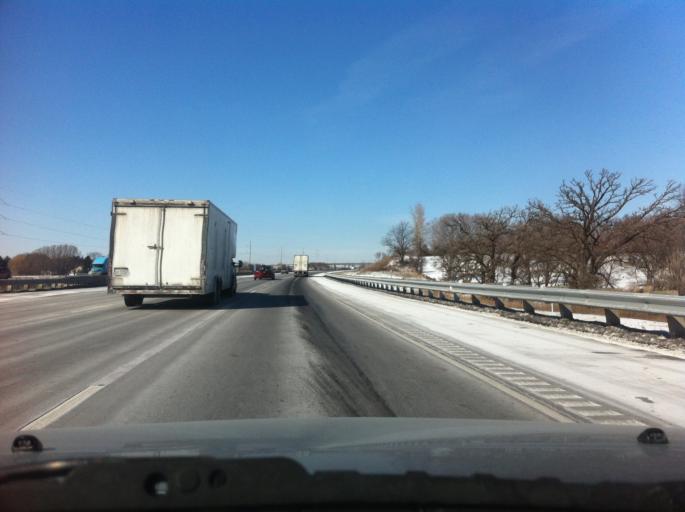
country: US
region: Wisconsin
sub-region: Dane County
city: Windsor
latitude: 43.2057
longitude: -89.3551
